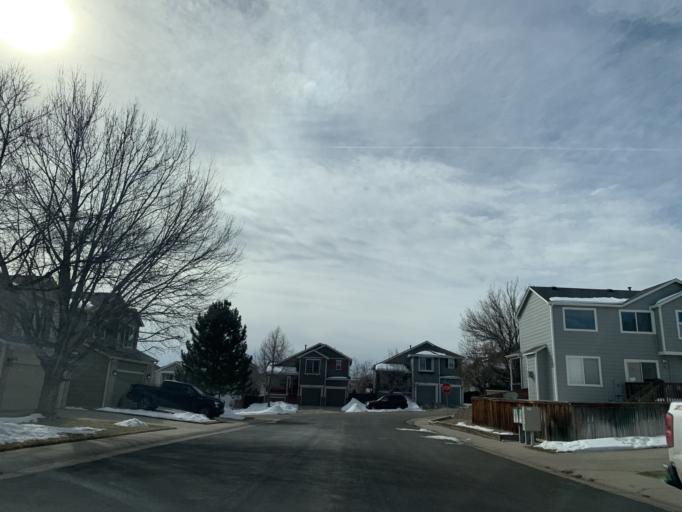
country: US
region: Colorado
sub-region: Douglas County
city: Carriage Club
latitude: 39.5399
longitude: -104.9284
